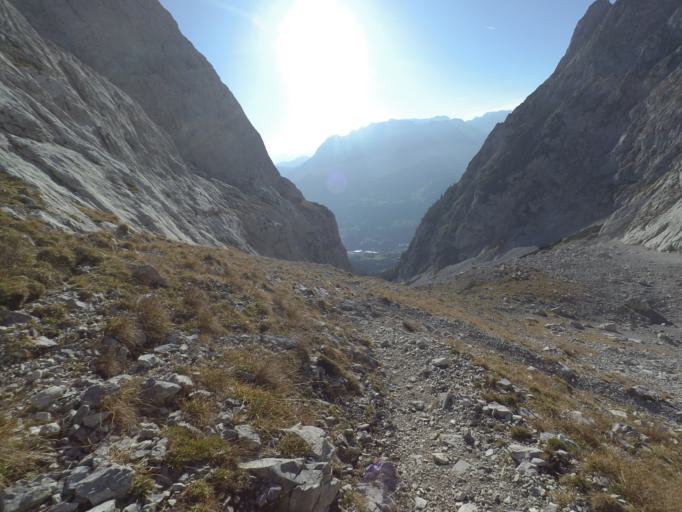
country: AT
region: Salzburg
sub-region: Politischer Bezirk Sankt Johann im Pongau
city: Werfenweng
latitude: 47.4952
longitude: 13.2360
